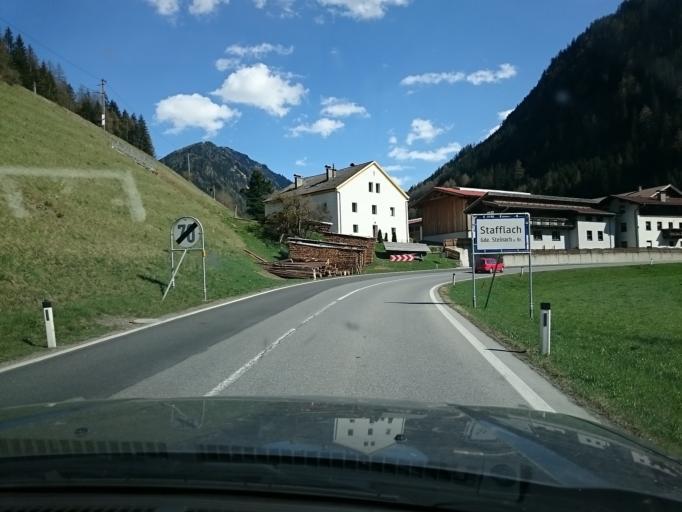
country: AT
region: Tyrol
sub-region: Politischer Bezirk Innsbruck Land
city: Gries am Brenner
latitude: 47.0654
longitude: 11.4877
